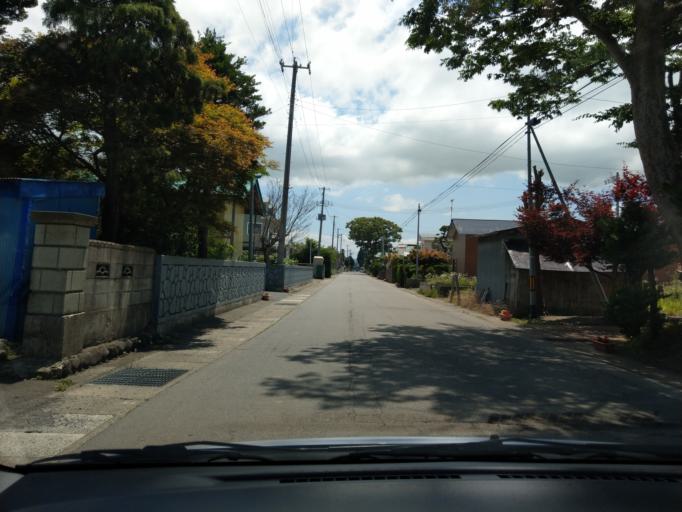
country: JP
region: Aomori
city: Namioka
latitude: 40.6814
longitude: 140.5601
